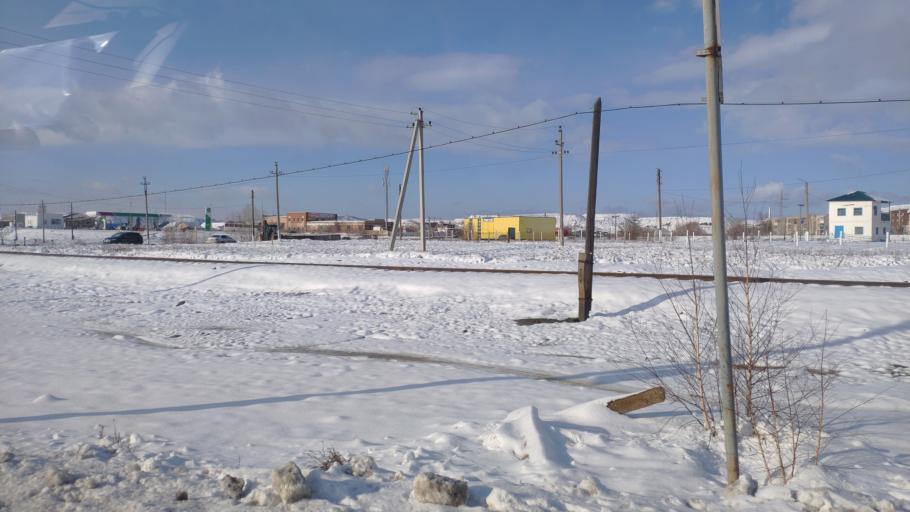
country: RU
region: Bashkortostan
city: Sibay
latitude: 52.7043
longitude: 58.6642
